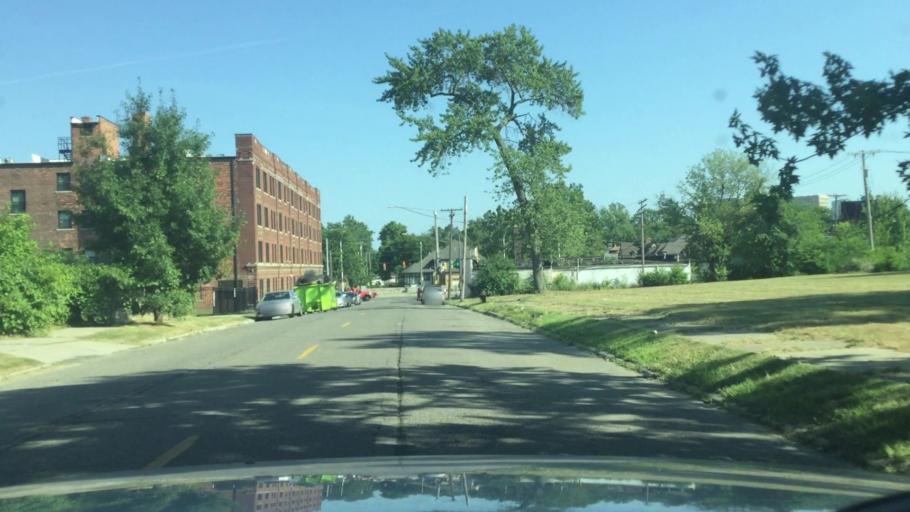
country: US
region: Michigan
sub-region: Wayne County
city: Grosse Pointe Park
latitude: 42.3601
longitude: -82.9855
